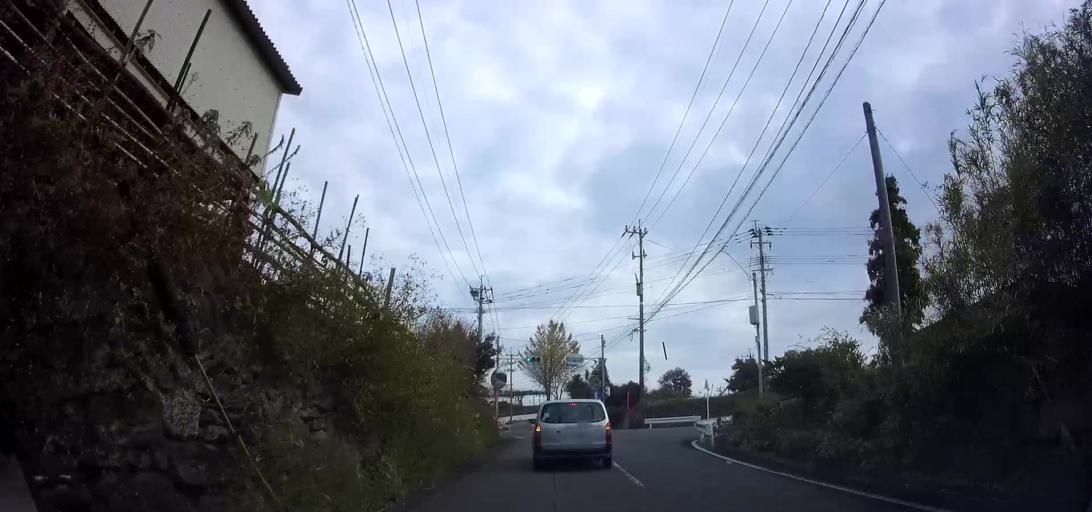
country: JP
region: Nagasaki
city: Shimabara
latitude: 32.6878
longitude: 130.2943
